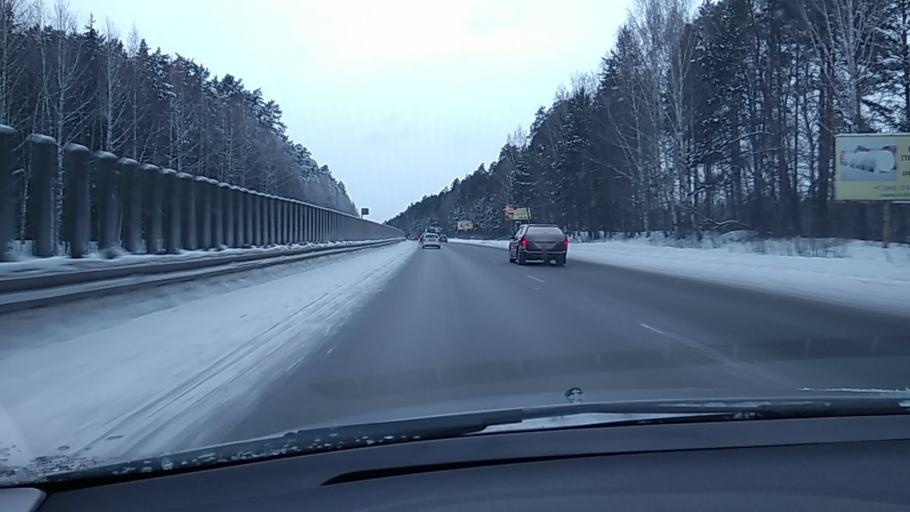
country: RU
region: Sverdlovsk
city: Istok
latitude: 56.7955
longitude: 60.8198
